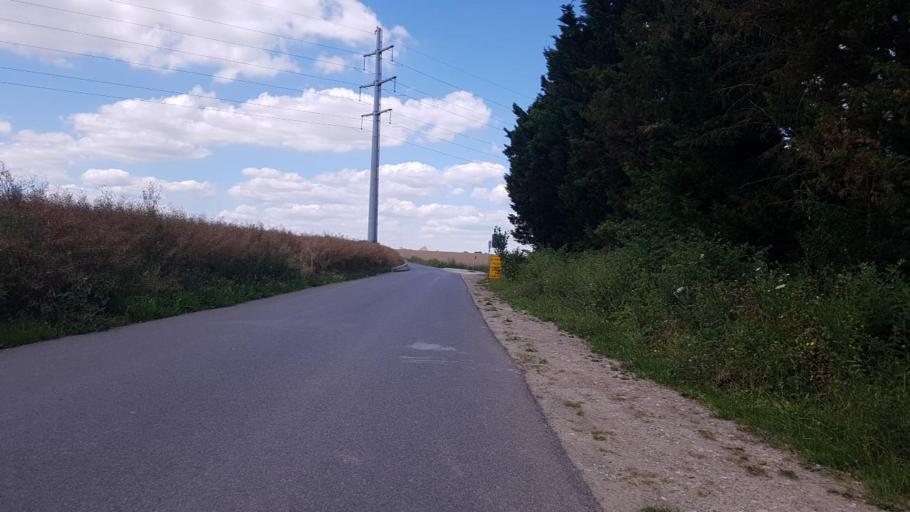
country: FR
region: Ile-de-France
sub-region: Departement de Seine-et-Marne
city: Claye-Souilly
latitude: 48.9782
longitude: 2.6683
